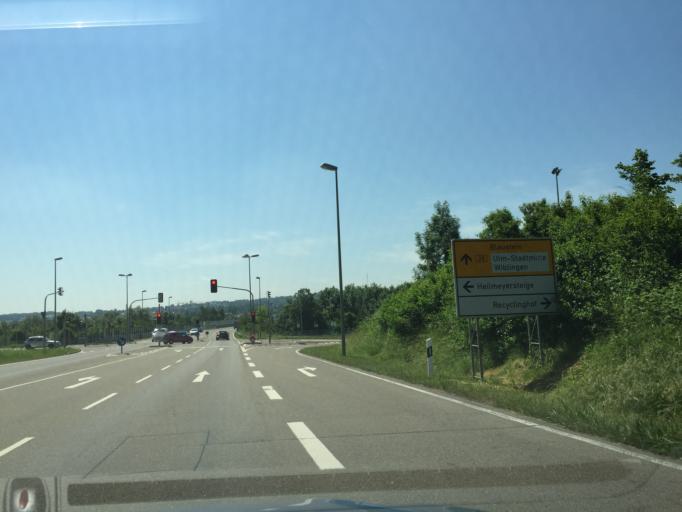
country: DE
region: Baden-Wuerttemberg
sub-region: Tuebingen Region
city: Ulm
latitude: 48.4080
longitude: 9.9467
